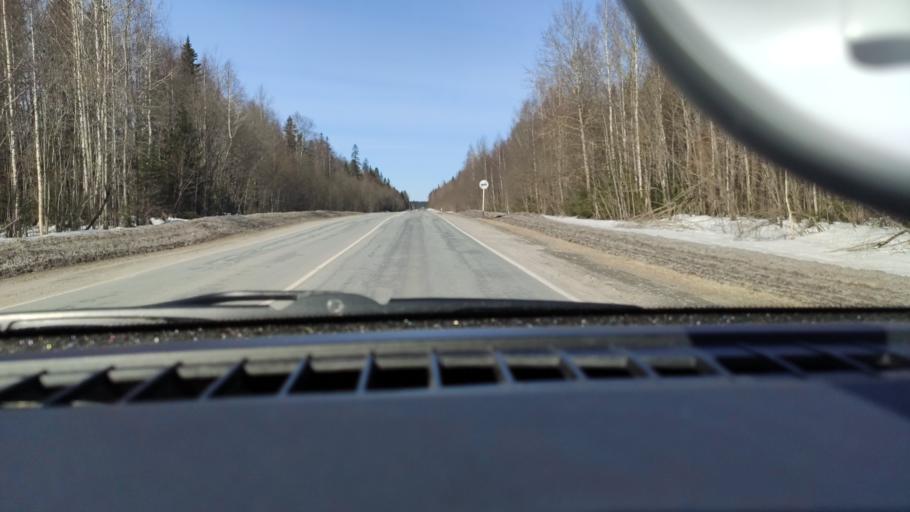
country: RU
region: Perm
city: Perm
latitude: 58.1798
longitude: 56.2258
